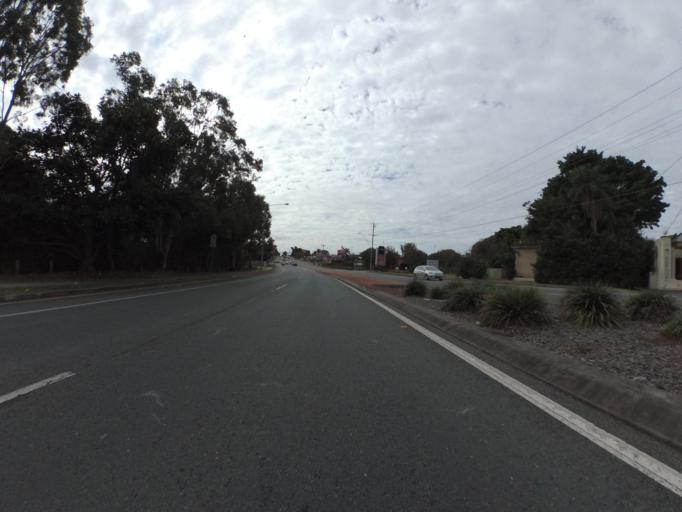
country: AU
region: Queensland
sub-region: Brisbane
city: Wynnum West
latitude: -27.4586
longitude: 153.1520
